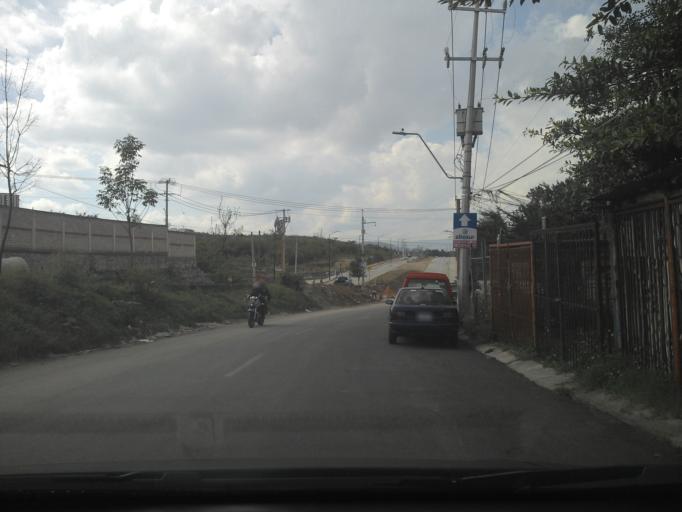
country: MX
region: Jalisco
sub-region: Tlajomulco de Zuniga
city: Altus Bosques
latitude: 20.6139
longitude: -103.3542
